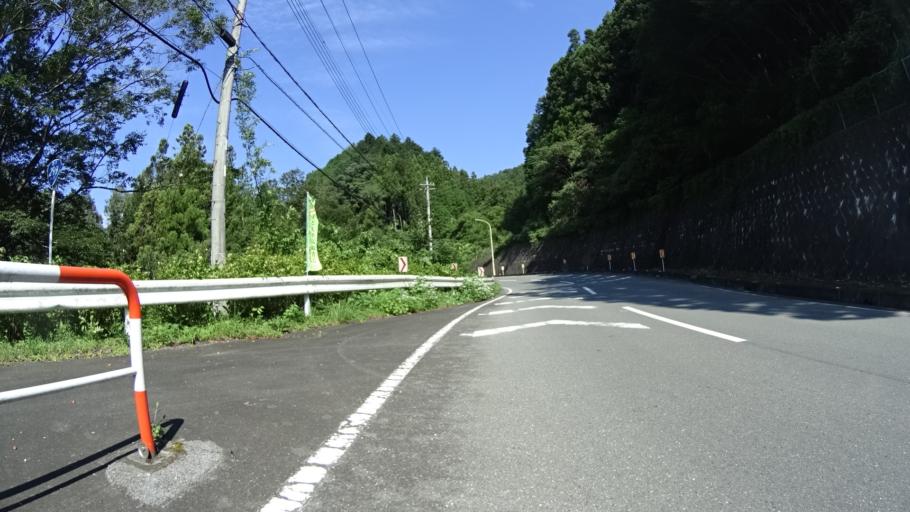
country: JP
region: Saitama
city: Chichibu
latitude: 36.0246
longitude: 138.9644
